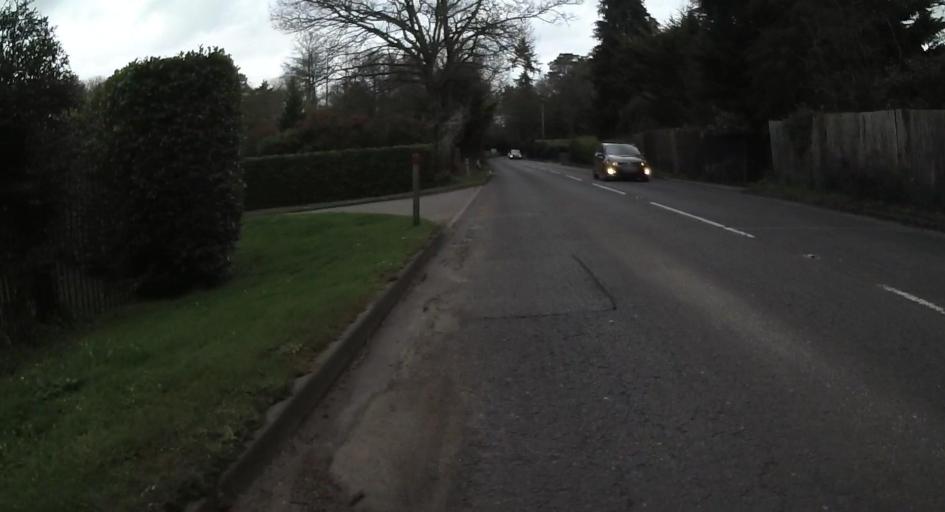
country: GB
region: England
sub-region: Surrey
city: Farnham
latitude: 51.1816
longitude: -0.7915
